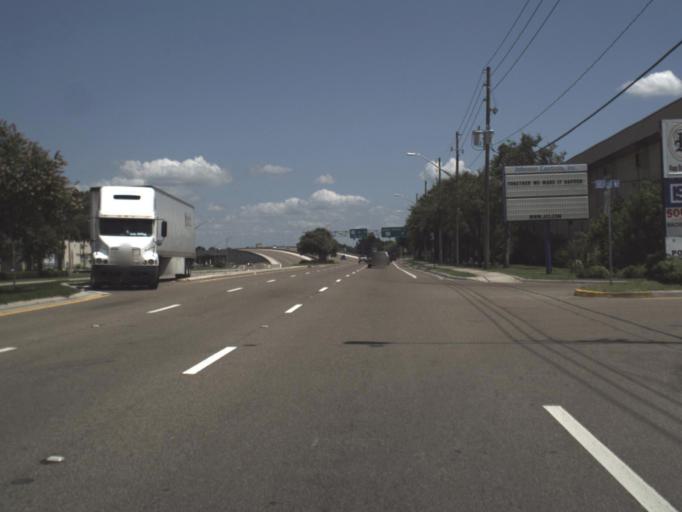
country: US
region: Florida
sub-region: Pinellas County
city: Pinellas Park
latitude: 27.8720
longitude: -82.7354
